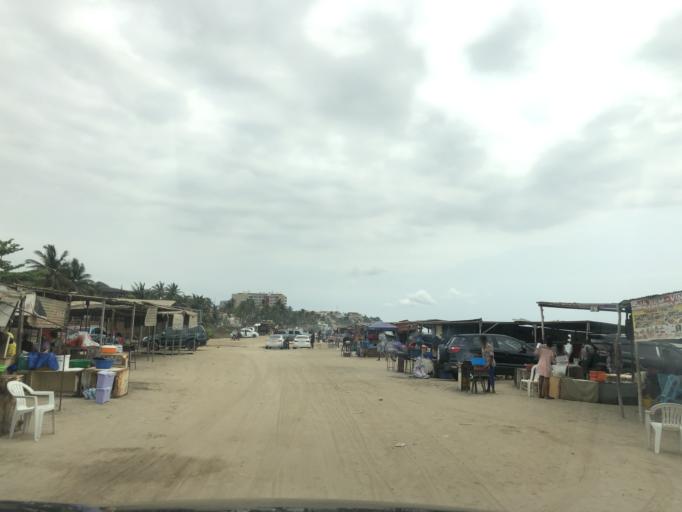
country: AO
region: Luanda
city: Luanda
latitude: -8.8725
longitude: 13.1933
